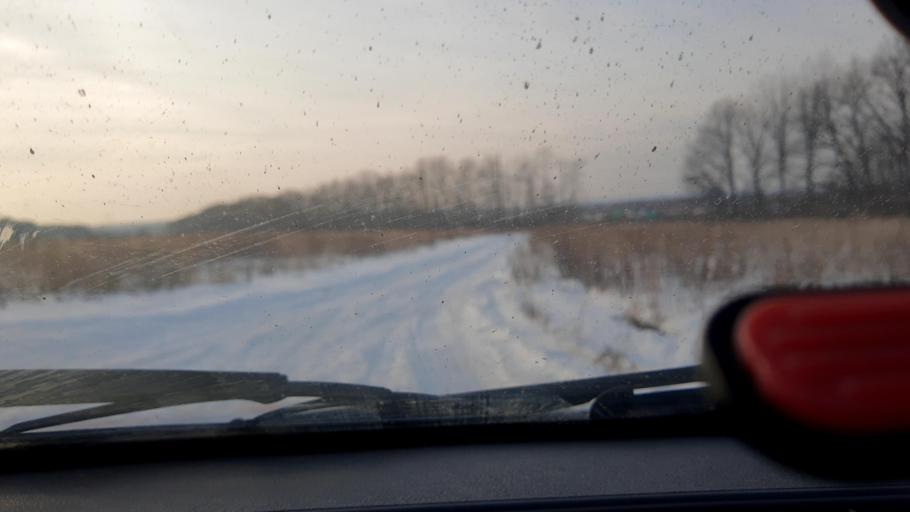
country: RU
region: Bashkortostan
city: Iglino
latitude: 54.7318
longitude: 56.2385
